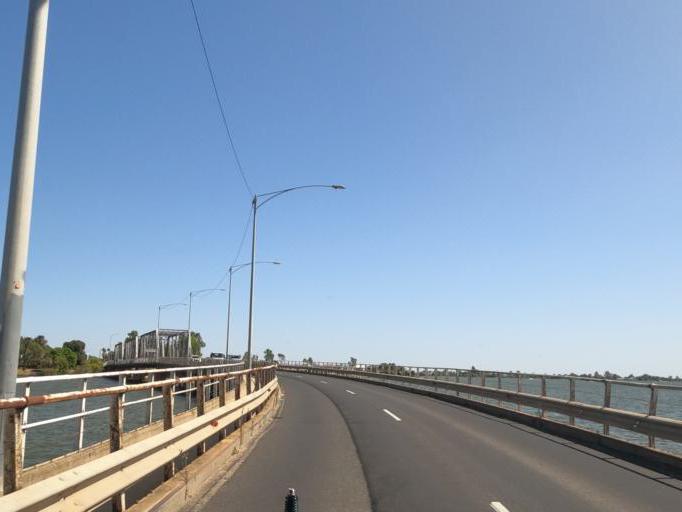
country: AU
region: New South Wales
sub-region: Corowa Shire
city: Mulwala
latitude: -36.0053
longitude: 146.0045
